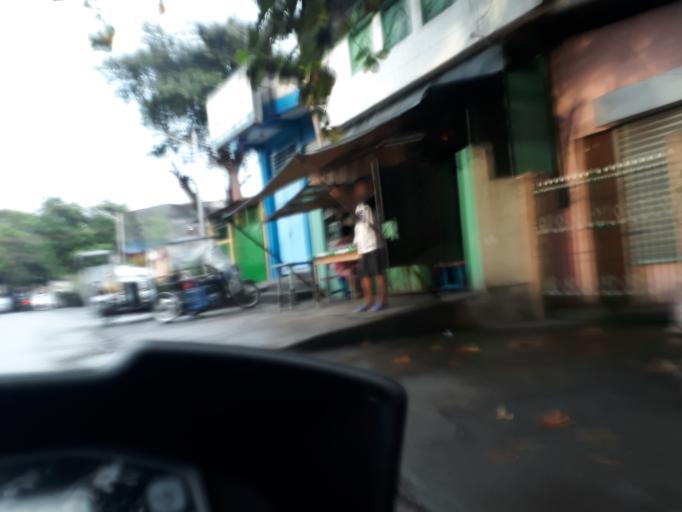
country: PH
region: Central Luzon
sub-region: Province of Bulacan
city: San Jose del Monte
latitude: 14.7746
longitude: 121.0499
